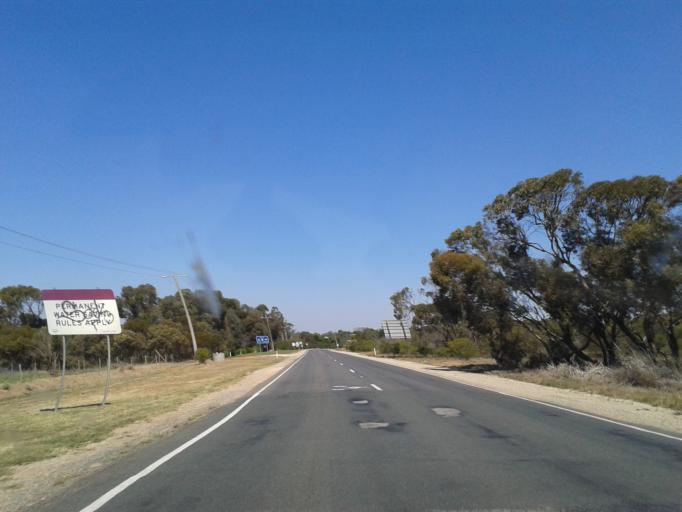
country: AU
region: Victoria
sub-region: Swan Hill
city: Swan Hill
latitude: -35.1646
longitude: 143.3757
